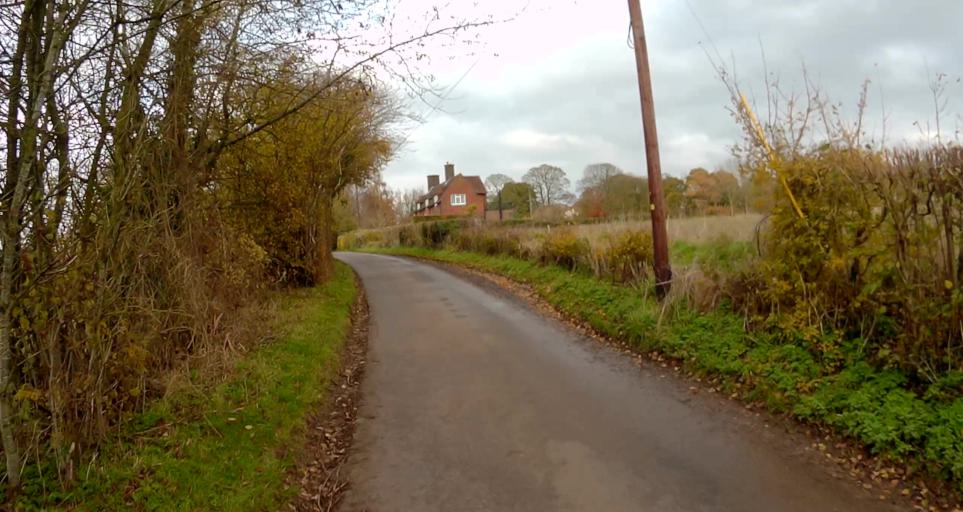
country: GB
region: England
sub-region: Hampshire
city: Long Sutton
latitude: 51.2076
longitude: -0.9409
